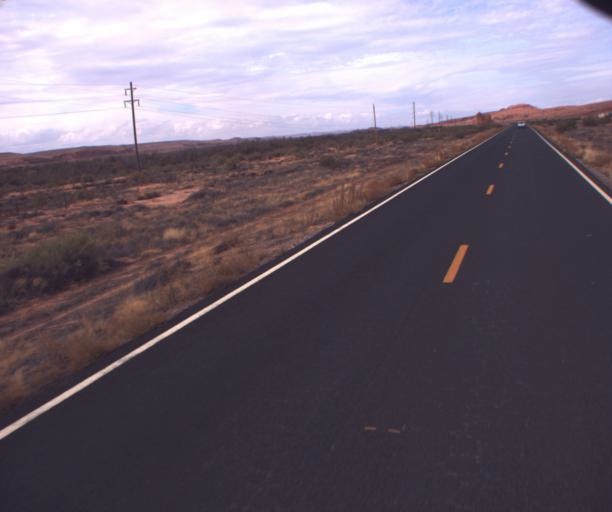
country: US
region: Arizona
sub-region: Apache County
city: Many Farms
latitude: 36.7317
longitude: -109.6323
